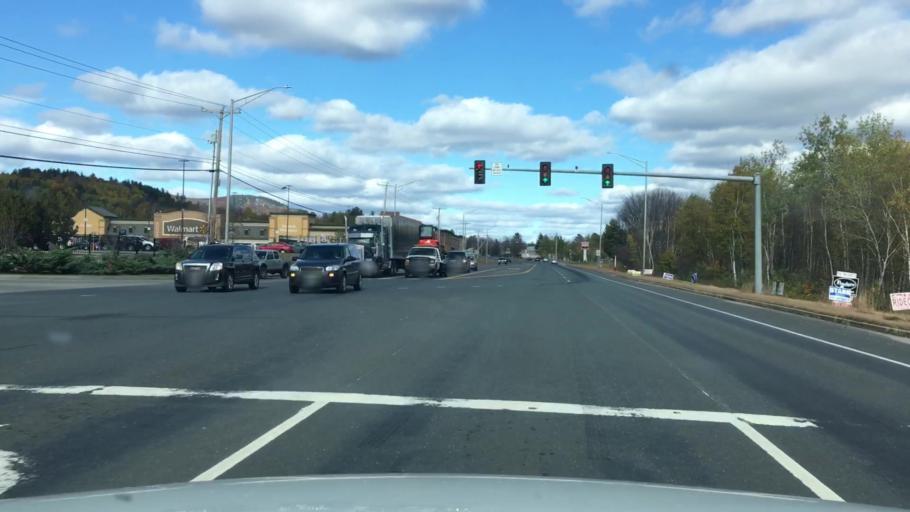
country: US
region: New Hampshire
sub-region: Coos County
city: Gorham
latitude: 44.4240
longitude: -71.1937
